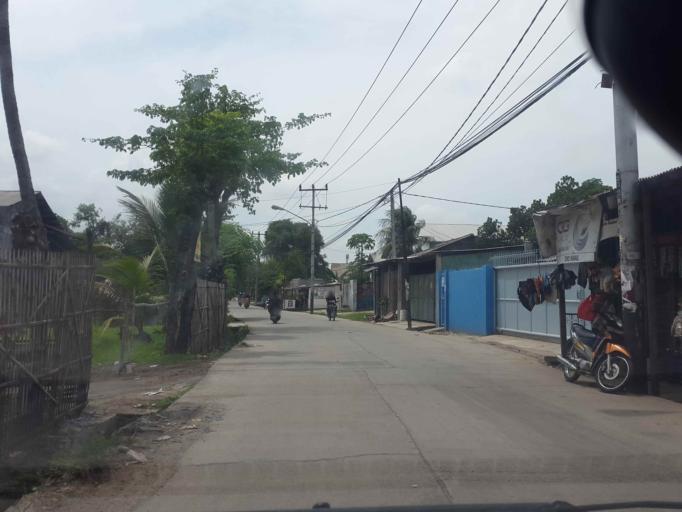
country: ID
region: West Java
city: Teluknaga
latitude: -6.1237
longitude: 106.6229
